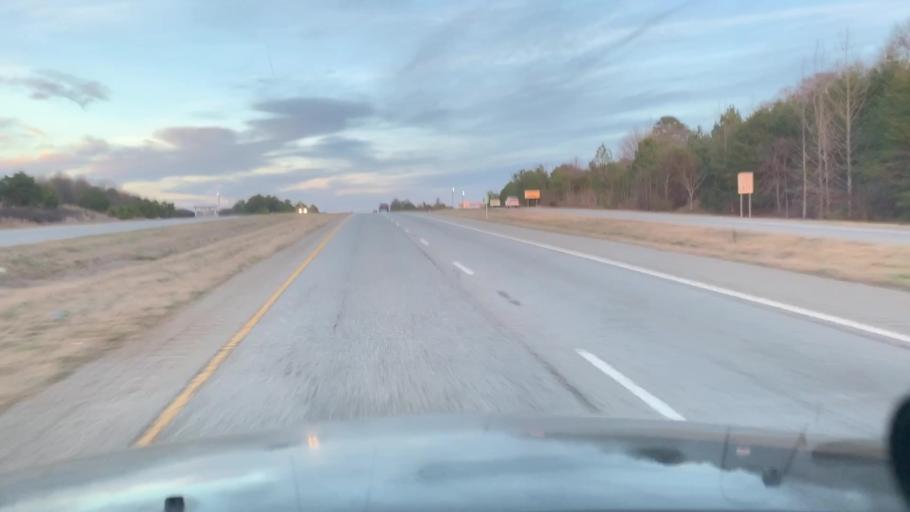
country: US
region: South Carolina
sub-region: Greenville County
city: Mauldin
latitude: 34.7220
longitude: -82.3465
